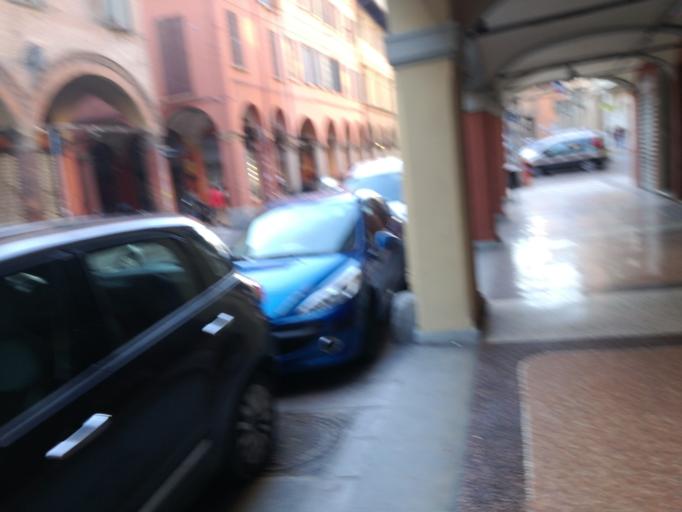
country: IT
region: Emilia-Romagna
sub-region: Provincia di Bologna
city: Bologna
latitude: 44.4905
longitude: 11.3562
